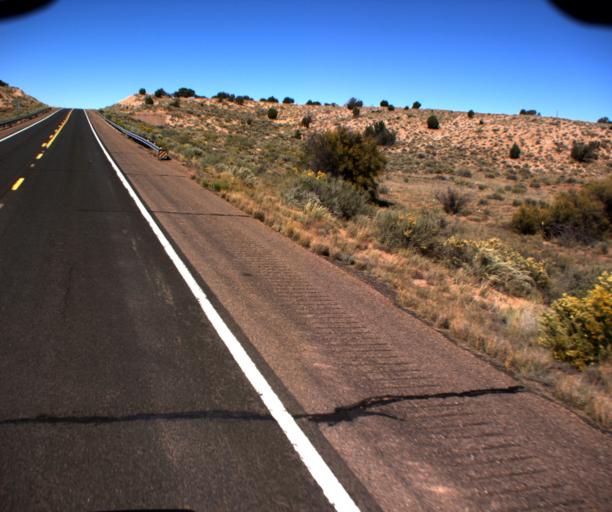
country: US
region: Arizona
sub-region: Navajo County
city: Snowflake
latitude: 34.6711
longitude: -109.7252
